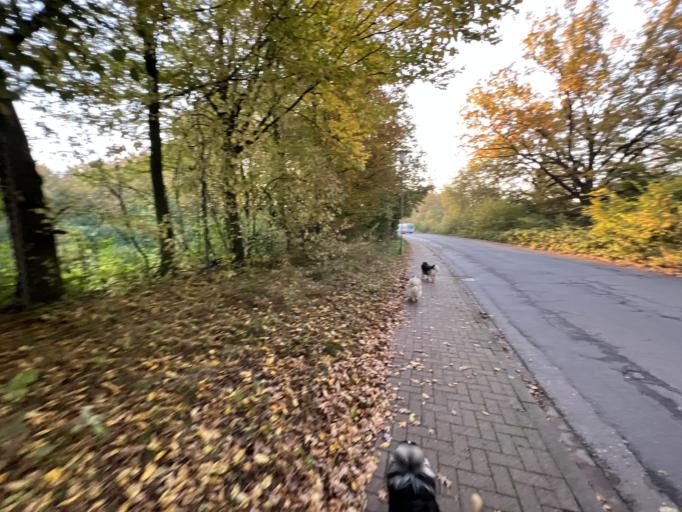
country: DE
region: Schleswig-Holstein
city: Stapelfeld
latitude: 53.6190
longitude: 10.2266
